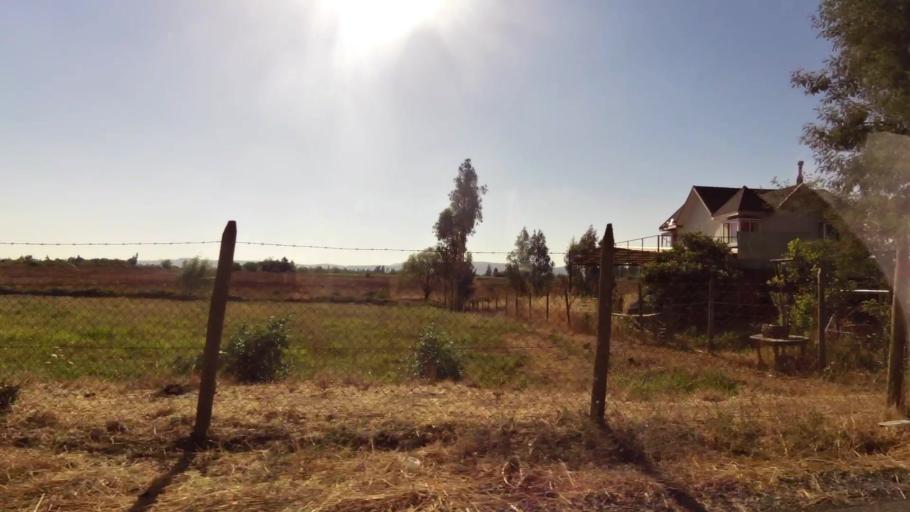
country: CL
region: Maule
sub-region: Provincia de Talca
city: Talca
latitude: -35.4096
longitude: -71.5916
